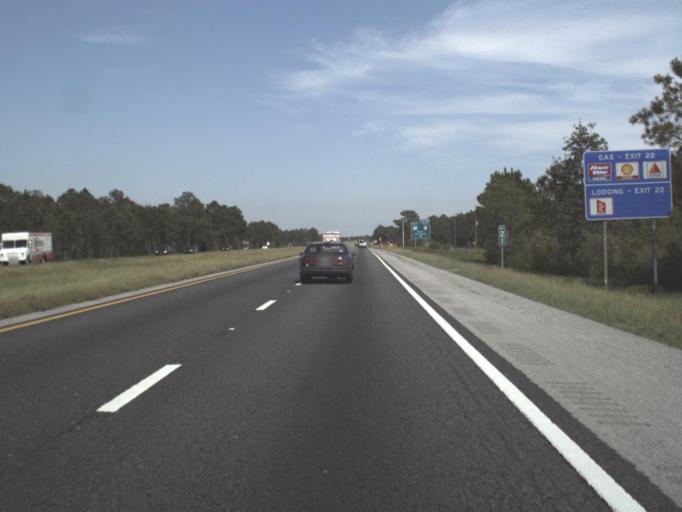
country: US
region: Florida
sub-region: Santa Rosa County
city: Pace
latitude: 30.5339
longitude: -87.0990
